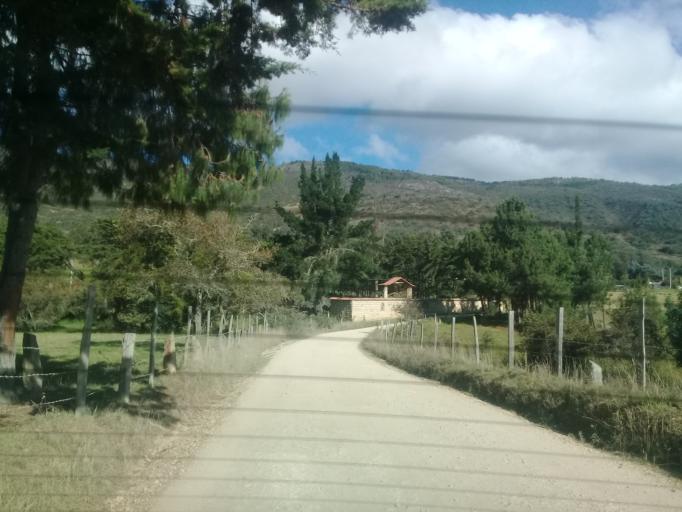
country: CO
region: Cundinamarca
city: Guatavita
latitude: 4.9335
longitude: -73.8792
